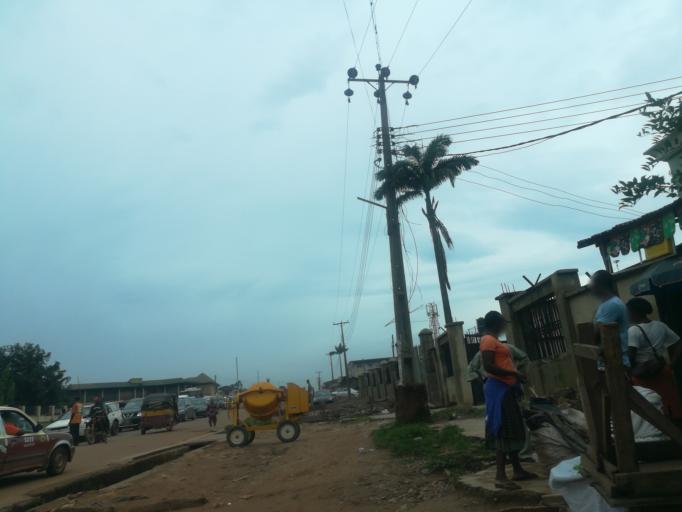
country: NG
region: Oyo
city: Ibadan
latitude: 7.3913
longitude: 3.9368
